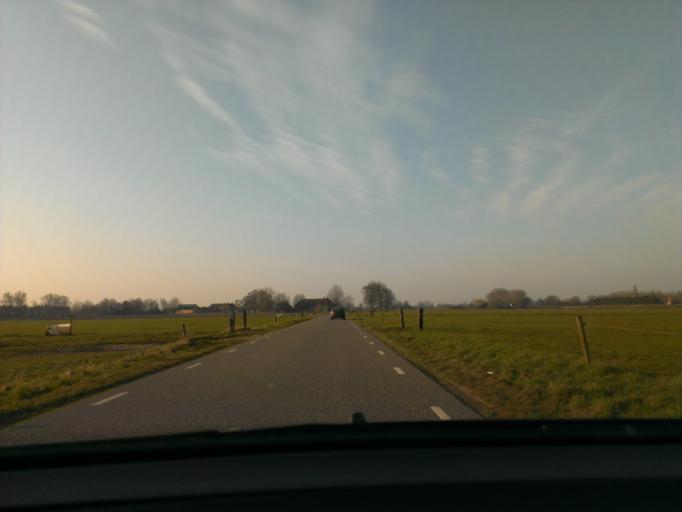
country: NL
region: Overijssel
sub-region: Gemeente Olst-Wijhe
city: Olst
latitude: 52.2900
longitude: 6.0952
